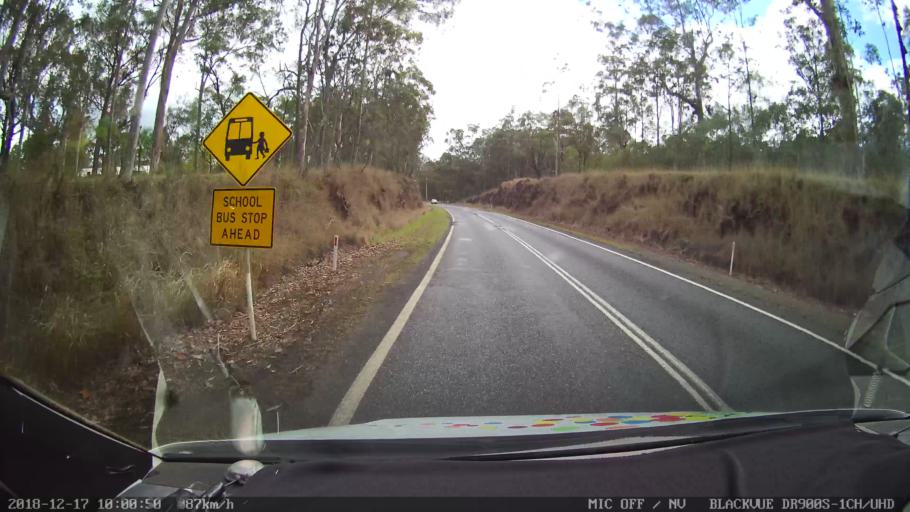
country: AU
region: New South Wales
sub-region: Tenterfield Municipality
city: Carrolls Creek
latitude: -28.9092
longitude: 152.4315
